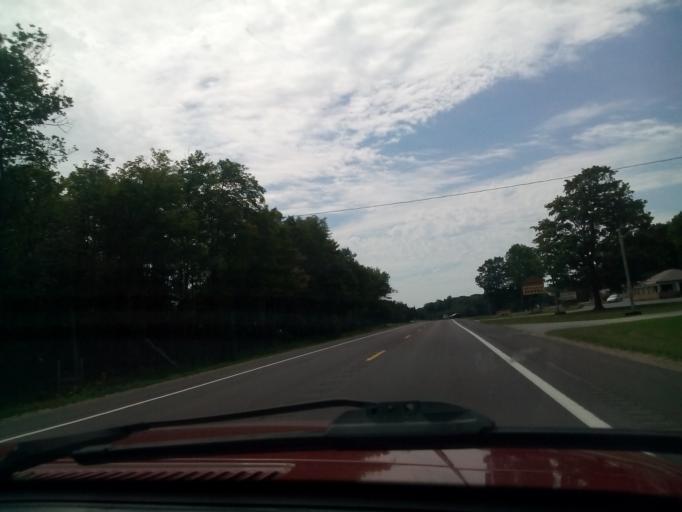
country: US
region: Michigan
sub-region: Schoolcraft County
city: Manistique
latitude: 46.0865
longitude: -85.9543
